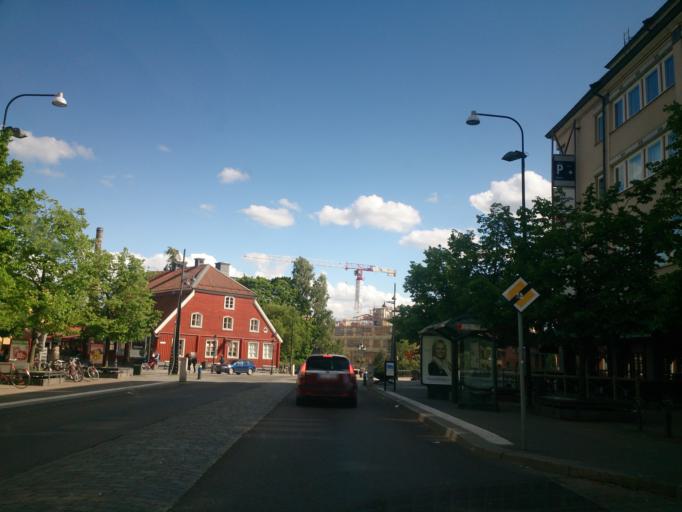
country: SE
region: OEstergoetland
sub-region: Norrkopings Kommun
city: Norrkoping
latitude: 58.5909
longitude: 16.1784
